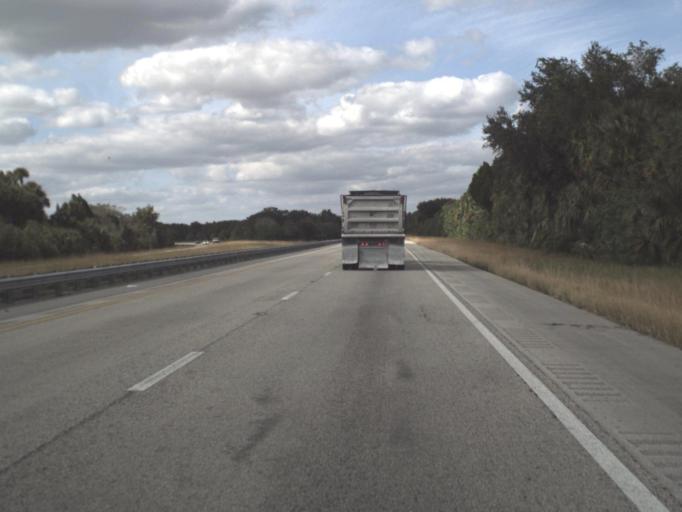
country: US
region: Florida
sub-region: Brevard County
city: Port Saint John
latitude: 28.4473
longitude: -80.8697
